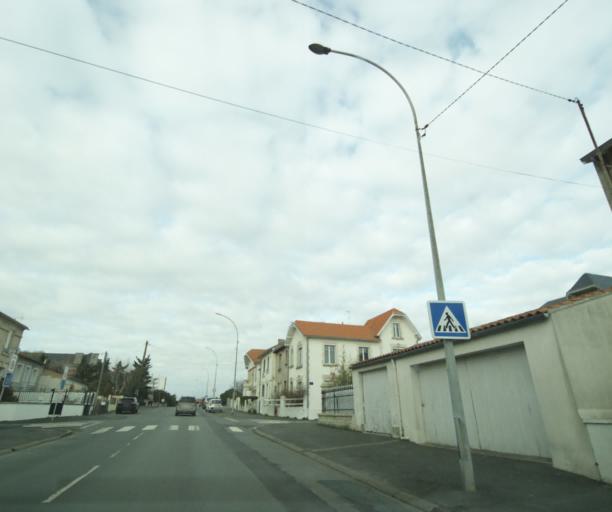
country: FR
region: Poitou-Charentes
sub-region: Departement de la Charente-Maritime
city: La Rochelle
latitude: 46.1646
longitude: -1.1647
